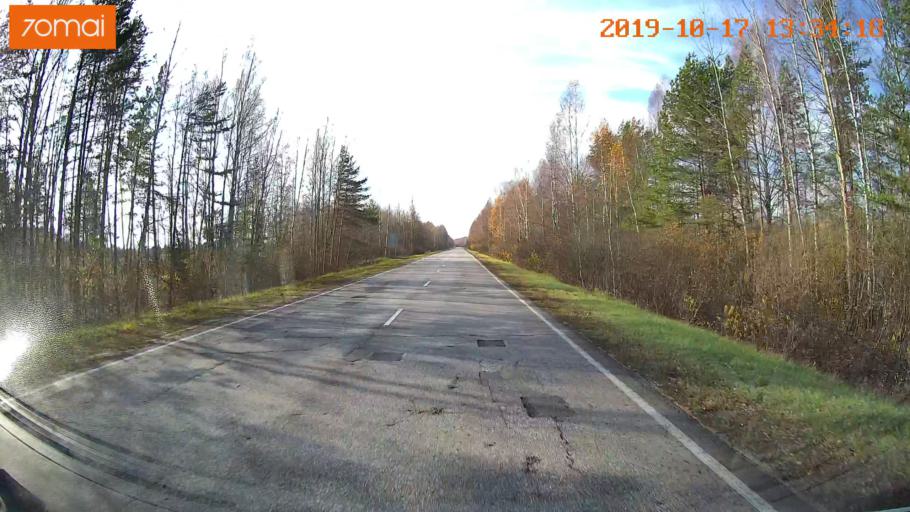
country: RU
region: Vladimir
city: Velikodvorskiy
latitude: 55.1443
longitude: 40.7193
